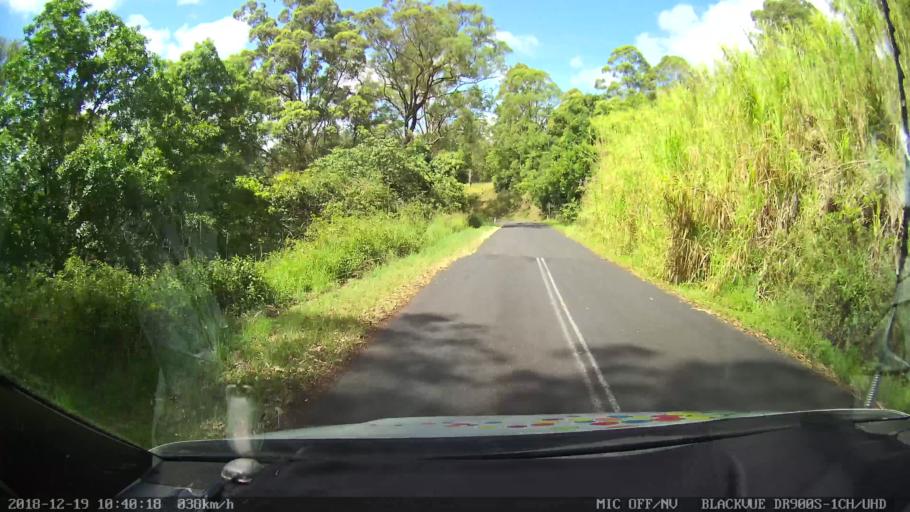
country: AU
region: New South Wales
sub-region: Lismore Municipality
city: Nimbin
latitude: -28.5841
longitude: 153.1593
